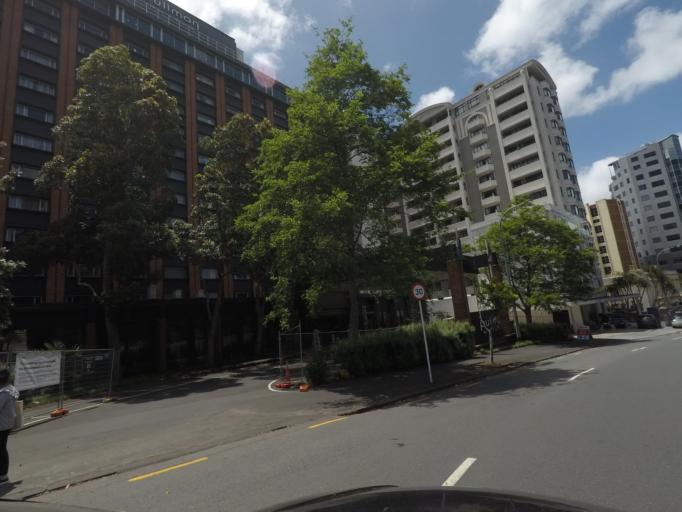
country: NZ
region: Auckland
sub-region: Auckland
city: Auckland
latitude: -36.8485
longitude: 174.7701
